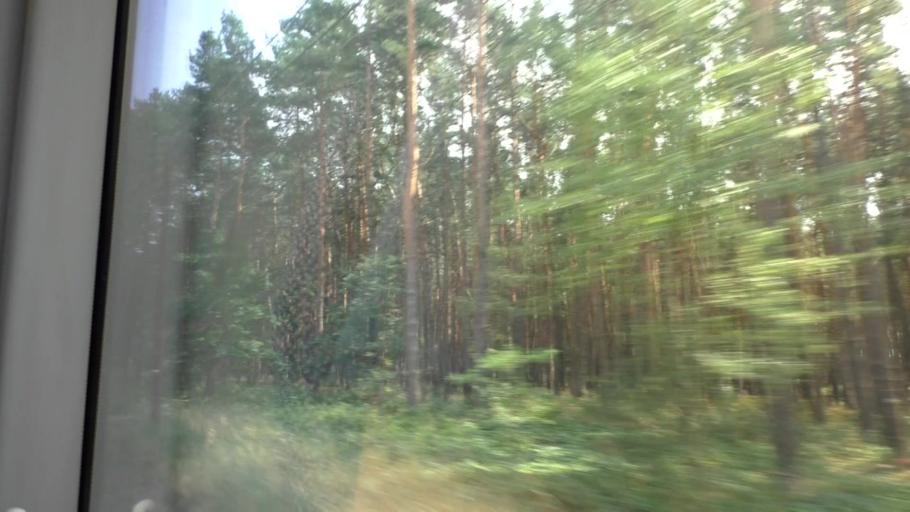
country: DE
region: Brandenburg
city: Wendisch Rietz
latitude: 52.1955
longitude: 14.0477
